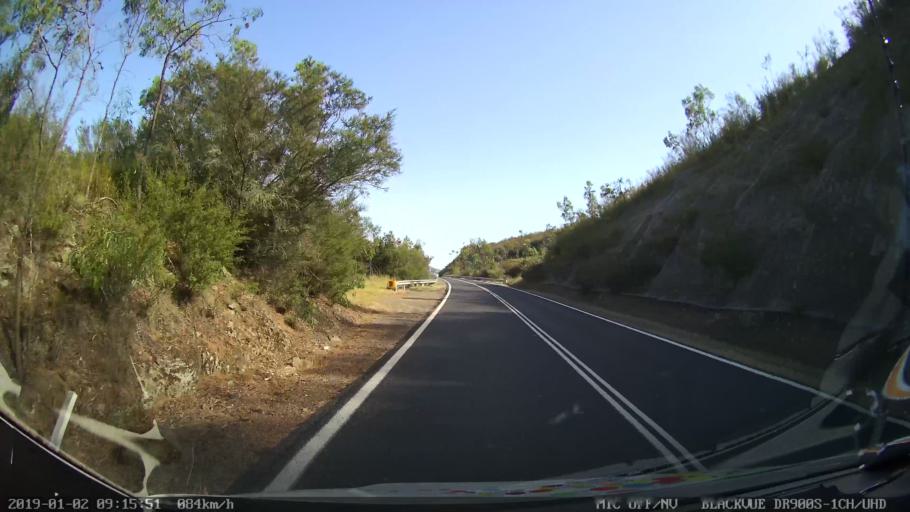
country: AU
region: New South Wales
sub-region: Tumut Shire
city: Tumut
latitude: -35.4601
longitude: 148.2819
